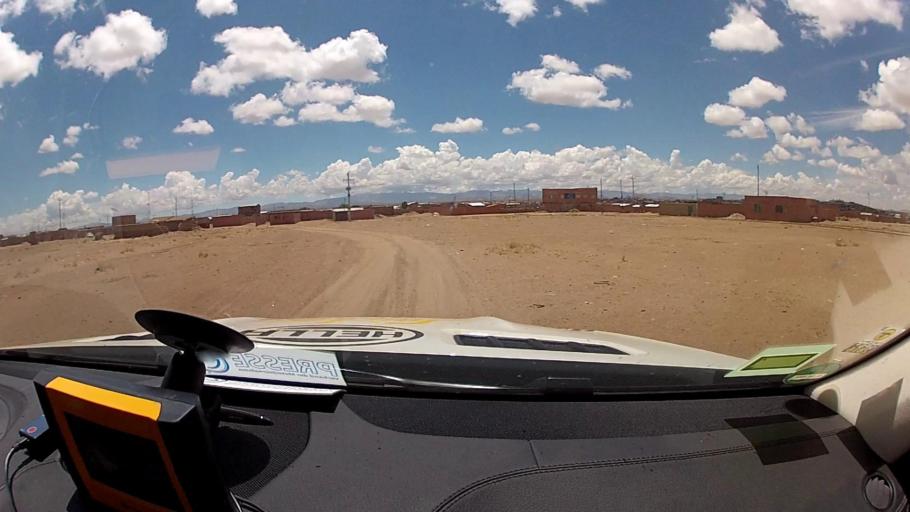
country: BO
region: Potosi
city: Villazon
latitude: -22.0810
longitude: -65.6111
